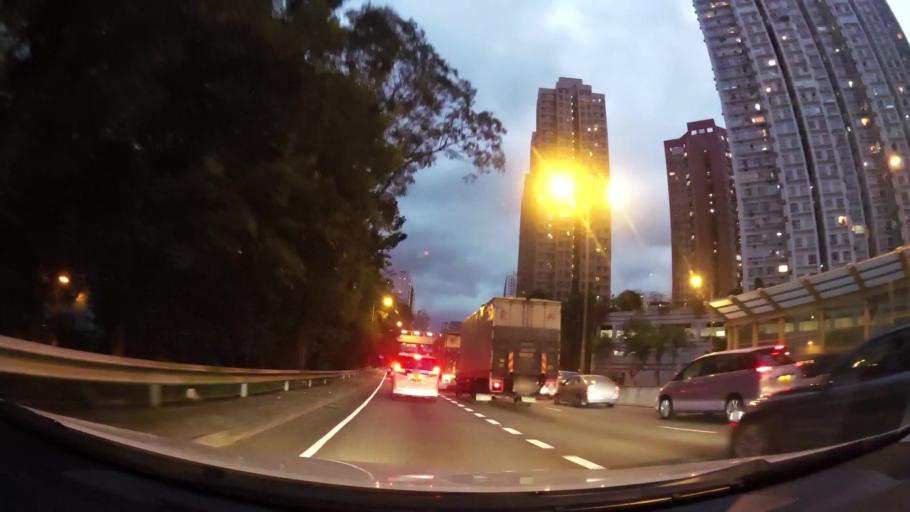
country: HK
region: Sha Tin
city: Sha Tin
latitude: 22.3797
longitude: 114.1856
